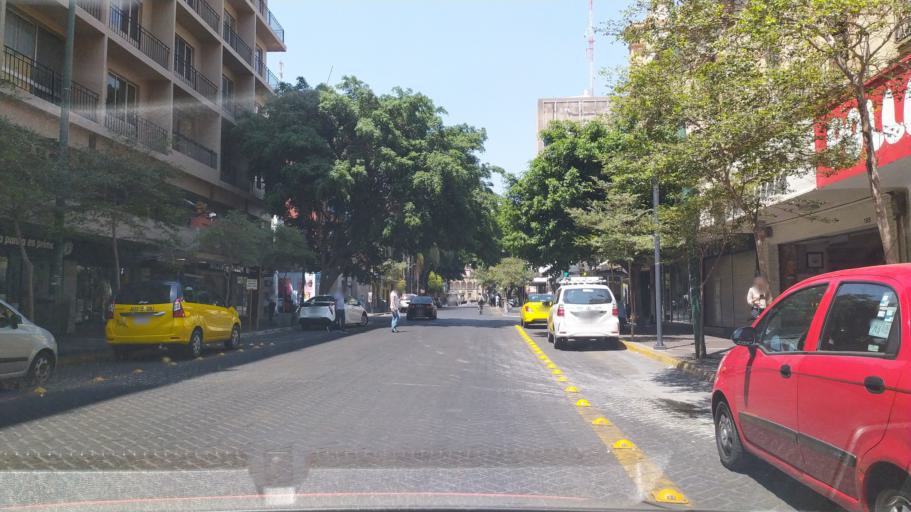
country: MX
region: Jalisco
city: Guadalajara
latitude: 20.6740
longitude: -103.3464
